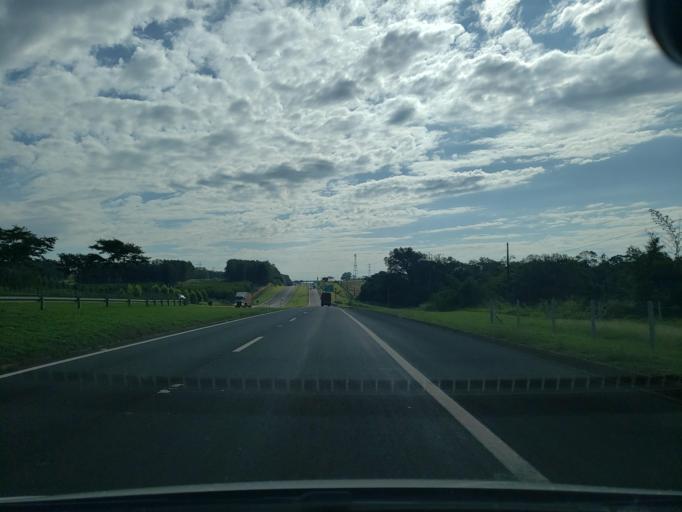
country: BR
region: Sao Paulo
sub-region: Lins
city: Lins
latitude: -21.6743
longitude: -49.7772
